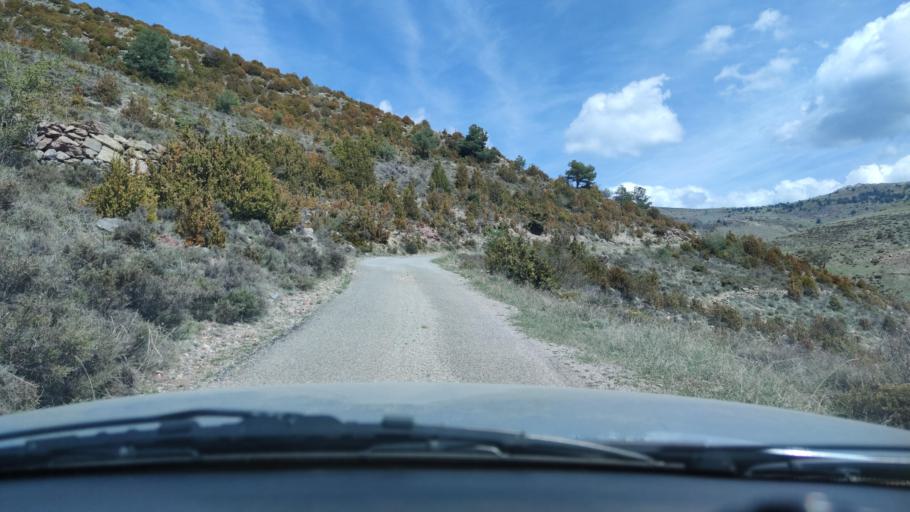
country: ES
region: Catalonia
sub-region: Provincia de Lleida
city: Sort
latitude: 42.3009
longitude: 1.1732
